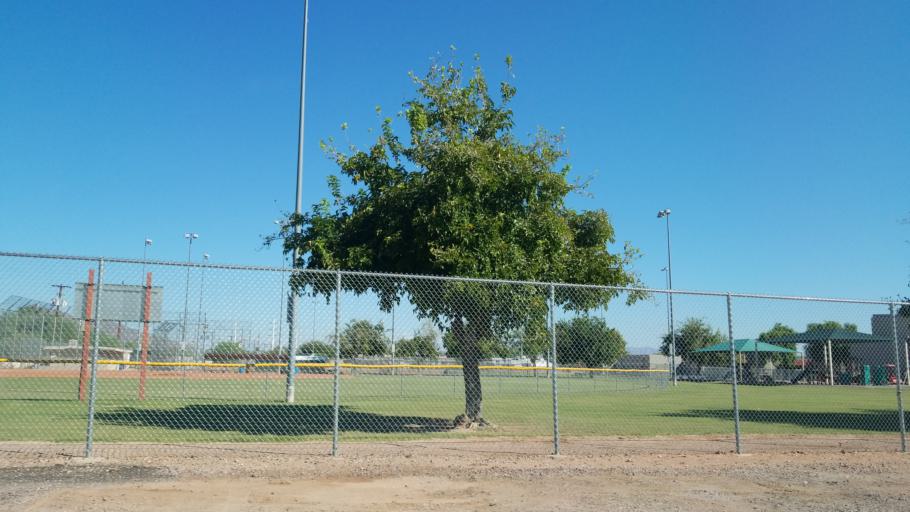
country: US
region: Arizona
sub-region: Maricopa County
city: Tempe Junction
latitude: 33.4584
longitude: -111.9390
